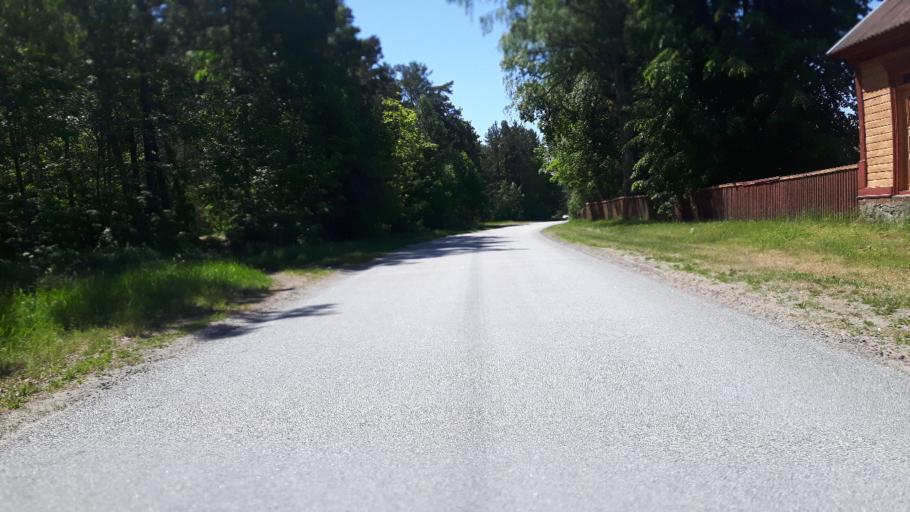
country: LV
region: Salacgrivas
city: Ainazi
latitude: 58.0374
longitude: 24.4638
